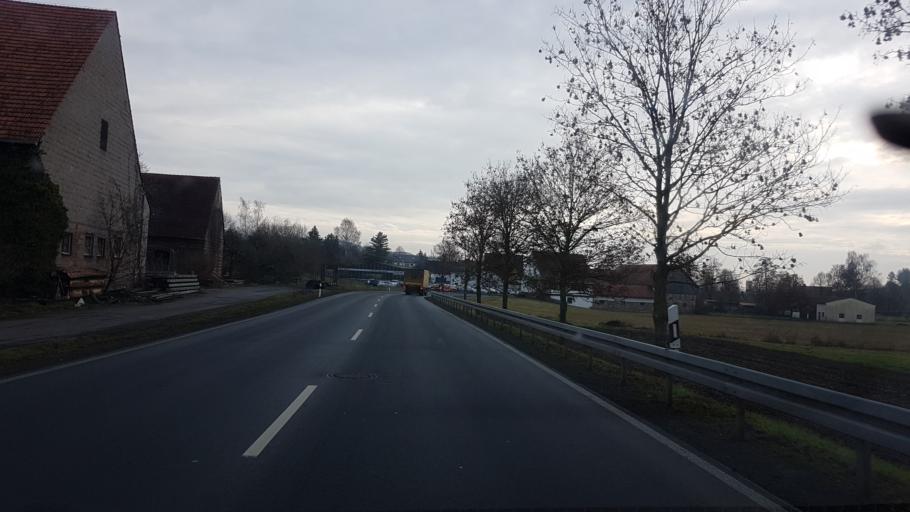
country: DE
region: Bavaria
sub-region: Regierungsbezirk Unterfranken
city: Pfarrweisach
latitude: 50.1633
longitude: 10.7248
